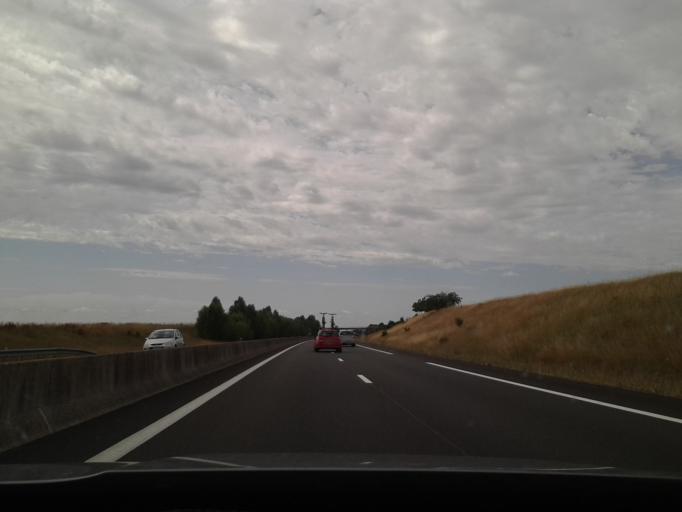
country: FR
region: Pays de la Loire
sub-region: Departement de la Sarthe
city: Beaumont-sur-Sarthe
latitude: 48.2659
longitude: 0.1622
